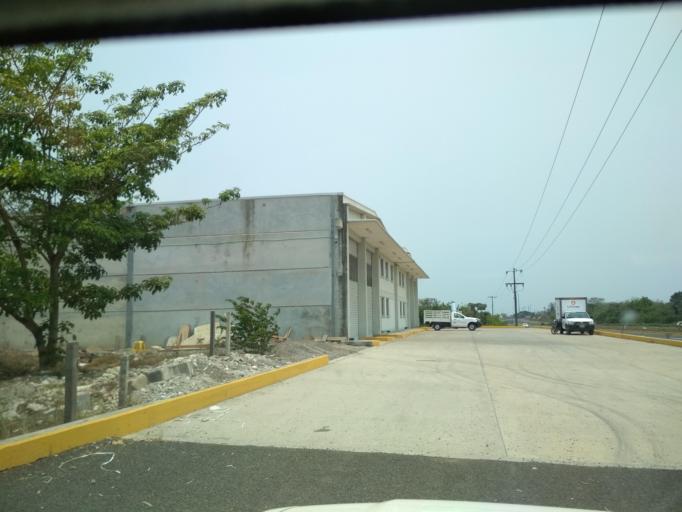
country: MX
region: Veracruz
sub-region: Veracruz
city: Delfino Victoria (Santa Fe)
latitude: 19.2221
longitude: -96.2583
